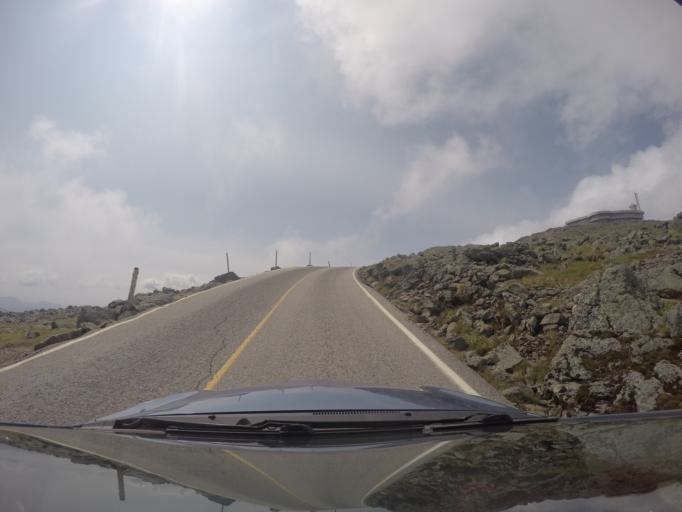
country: US
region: New Hampshire
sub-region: Coos County
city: Gorham
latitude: 44.2725
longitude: -71.3011
